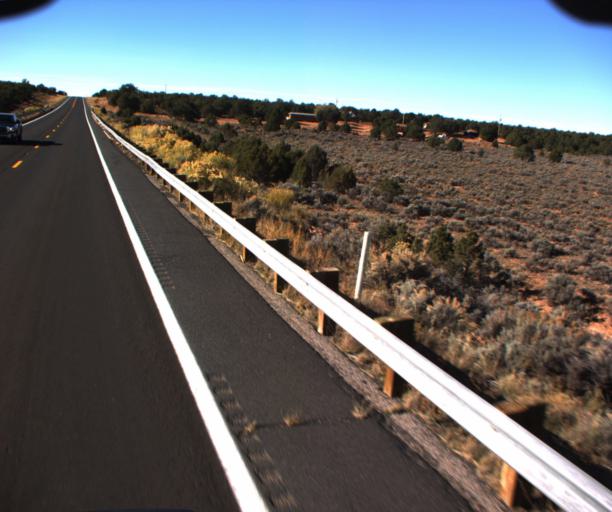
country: US
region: Arizona
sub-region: Coconino County
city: Kaibito
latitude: 36.5834
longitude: -110.8643
